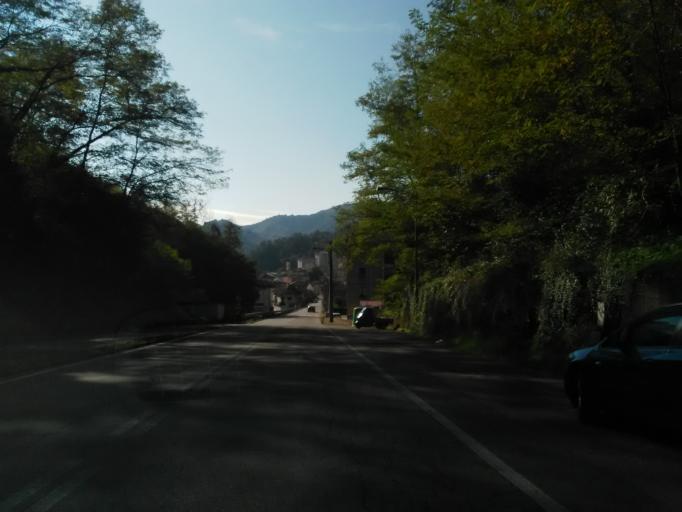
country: IT
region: Piedmont
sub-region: Provincia di Biella
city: Crevacuore
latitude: 45.6909
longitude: 8.2466
